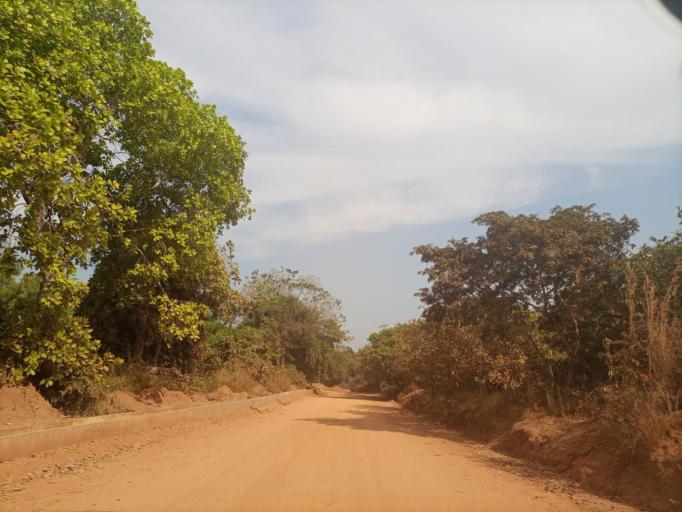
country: NG
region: Enugu
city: Opi
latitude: 6.8103
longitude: 7.5215
